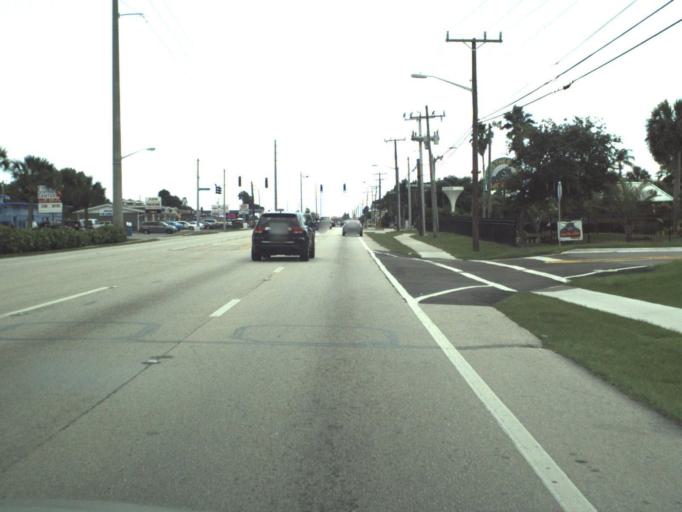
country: US
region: Florida
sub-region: Brevard County
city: Cape Canaveral
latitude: 28.3758
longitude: -80.6057
